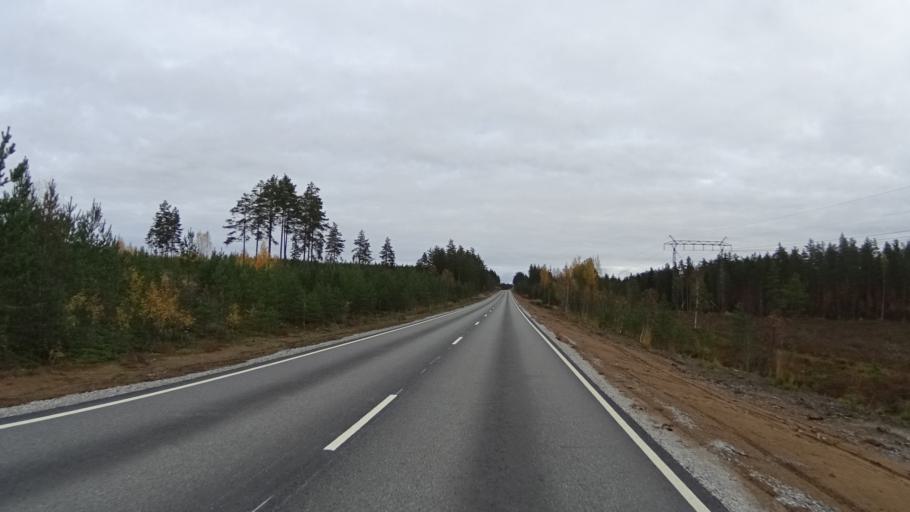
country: FI
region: South Karelia
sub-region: Lappeenranta
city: Lemi
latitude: 60.9817
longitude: 27.9010
